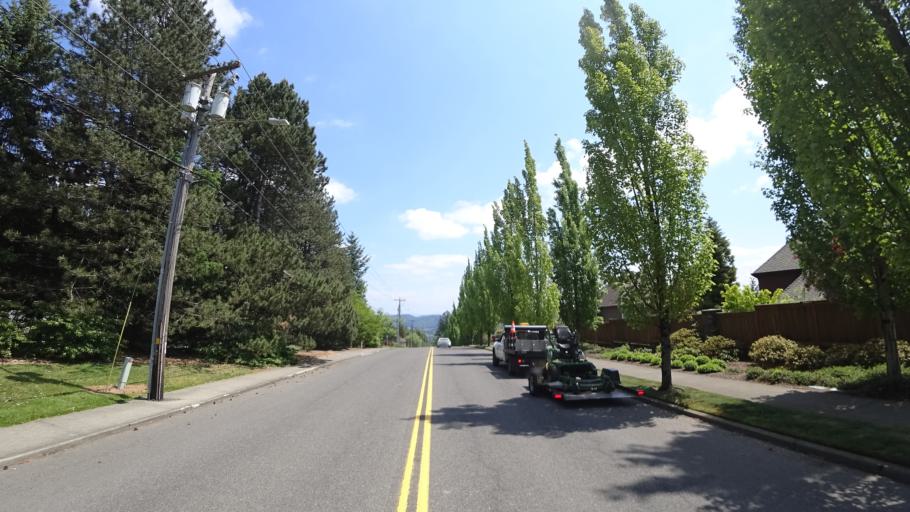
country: US
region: Oregon
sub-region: Clackamas County
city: Happy Valley
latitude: 45.4613
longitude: -122.5170
